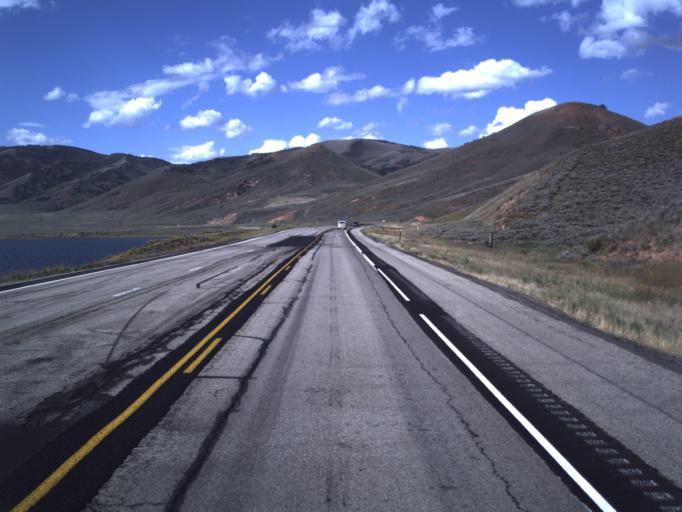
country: US
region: Utah
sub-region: Wasatch County
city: Heber
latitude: 40.2046
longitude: -111.1046
